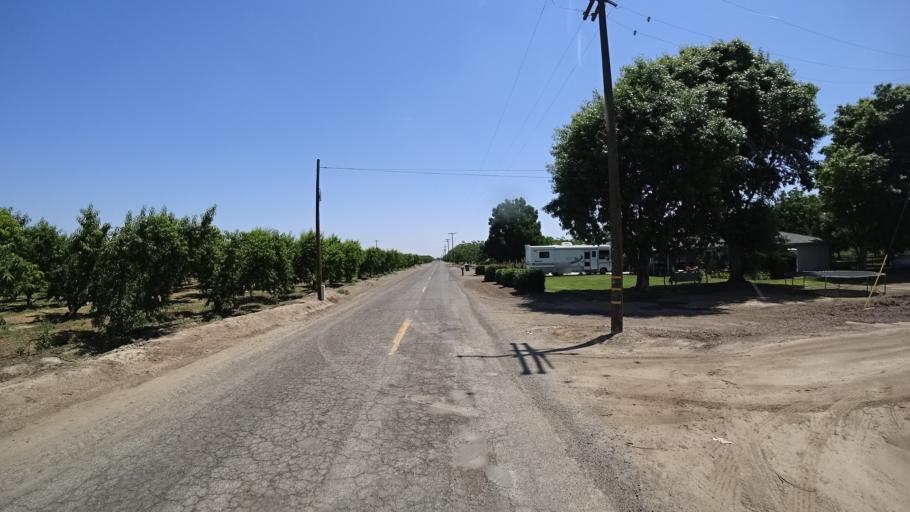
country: US
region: California
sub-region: Fresno County
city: Laton
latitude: 36.3864
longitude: -119.7566
